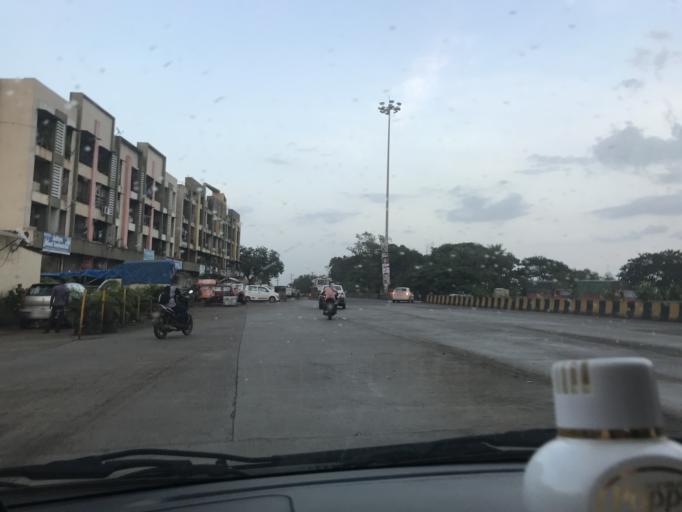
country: IN
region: Maharashtra
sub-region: Thane
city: Thane
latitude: 19.2351
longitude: 73.0131
